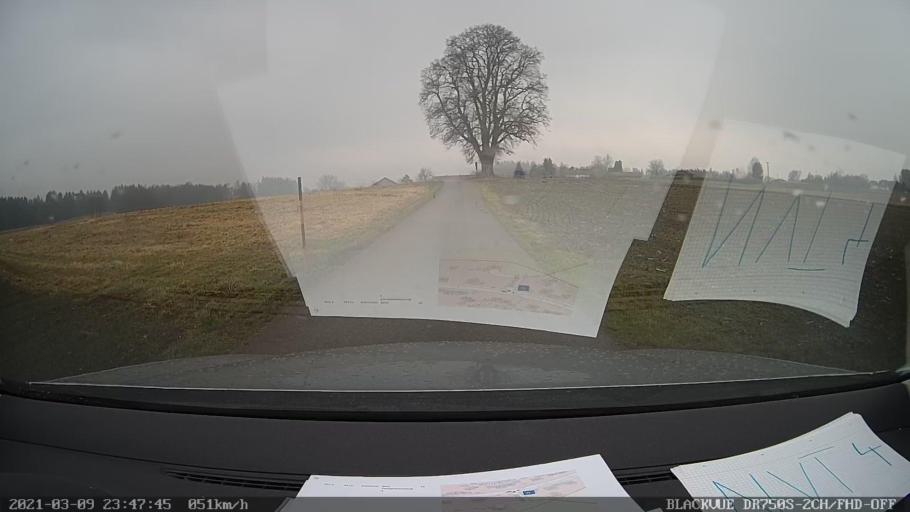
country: DE
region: Bavaria
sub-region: Upper Bavaria
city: Schonstett
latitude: 47.9815
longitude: 12.2565
